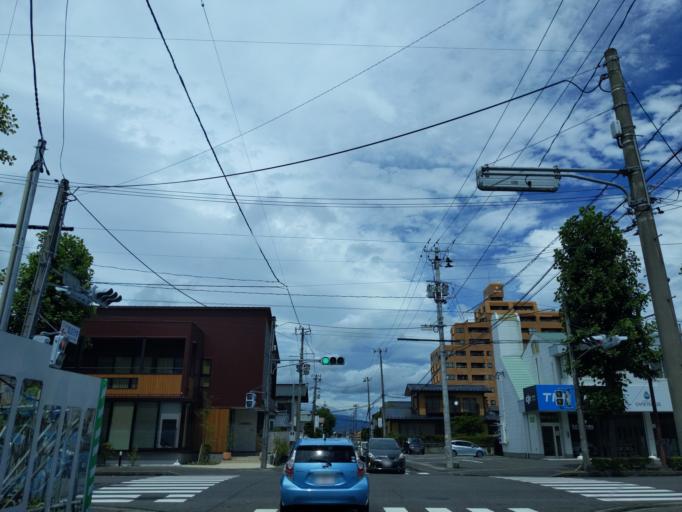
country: JP
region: Fukushima
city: Koriyama
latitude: 37.3985
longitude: 140.3501
